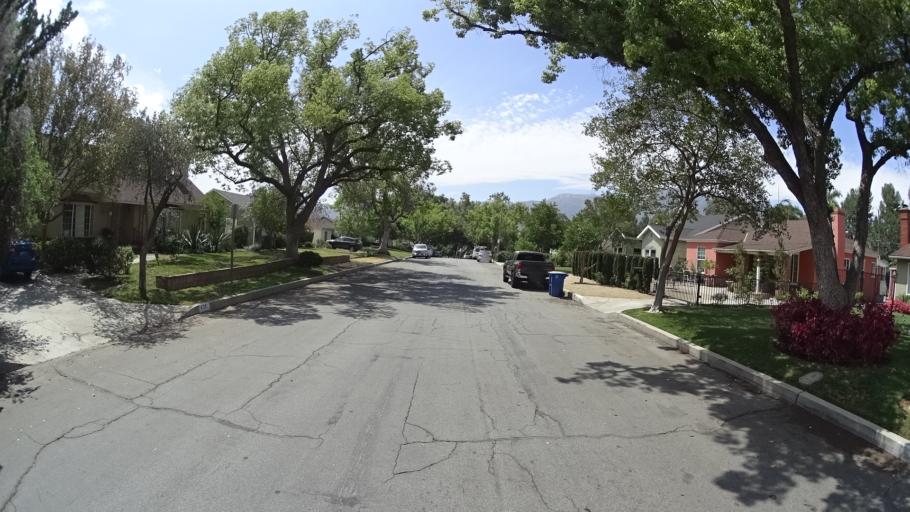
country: US
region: California
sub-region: Los Angeles County
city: Burbank
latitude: 34.1592
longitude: -118.3226
